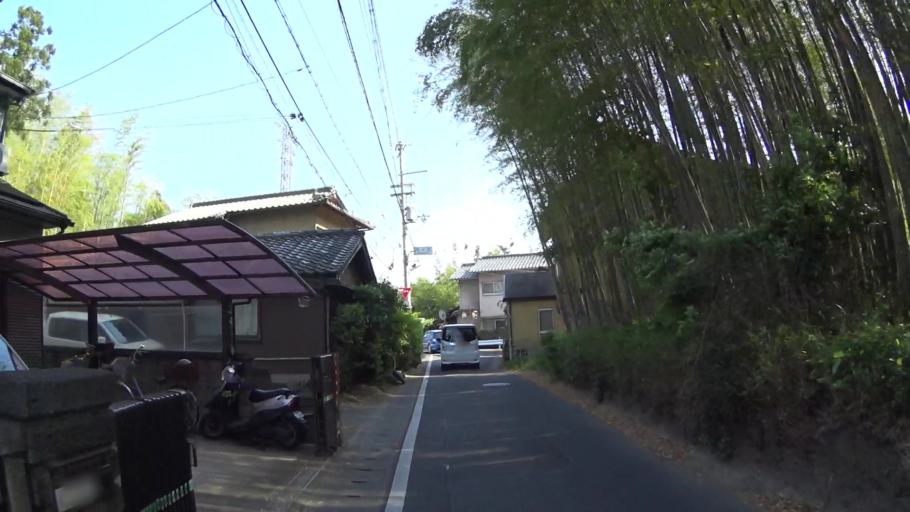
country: JP
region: Kyoto
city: Muko
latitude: 34.9455
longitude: 135.6771
